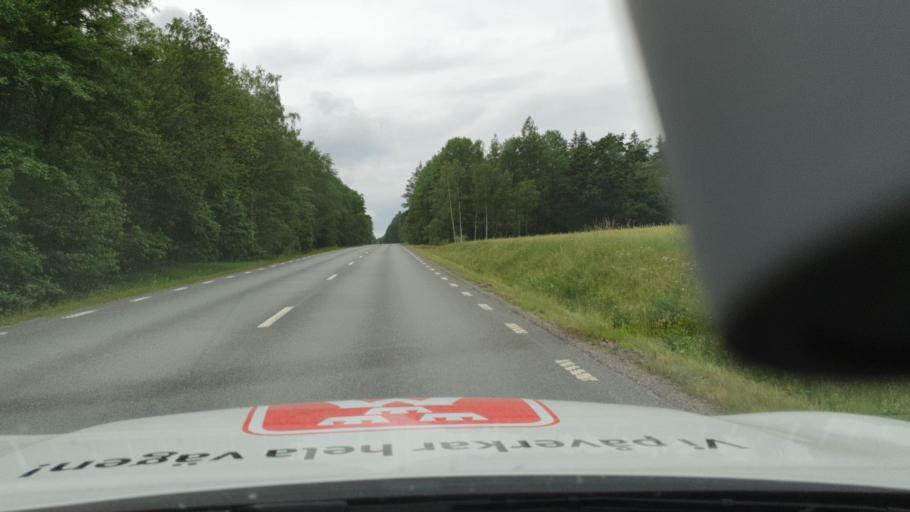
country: SE
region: Vaestra Goetaland
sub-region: Hjo Kommun
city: Hjo
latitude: 58.2266
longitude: 14.1786
